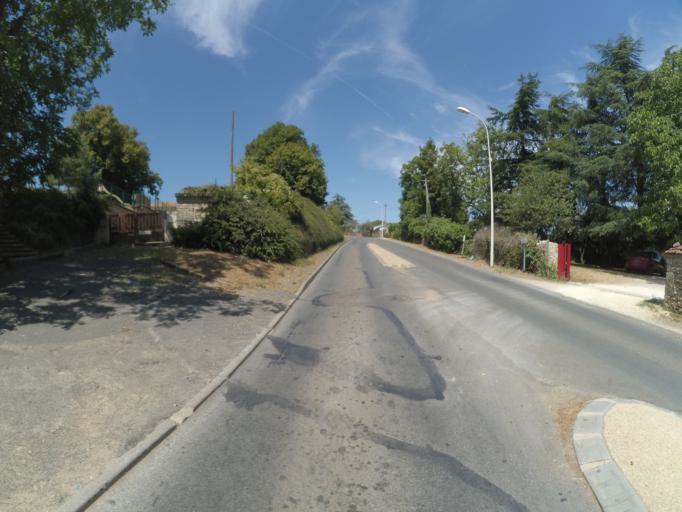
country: FR
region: Poitou-Charentes
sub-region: Departement de la Vienne
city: Vivonne
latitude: 46.4190
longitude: 0.3105
